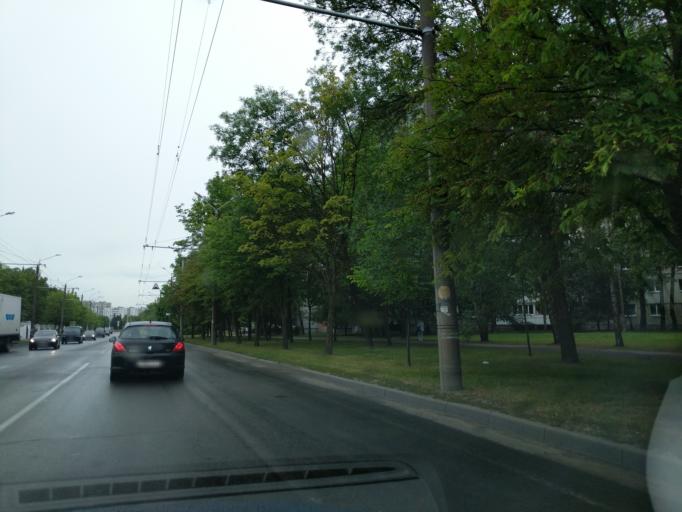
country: BY
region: Minsk
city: Novoye Medvezhino
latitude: 53.8600
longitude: 27.4766
